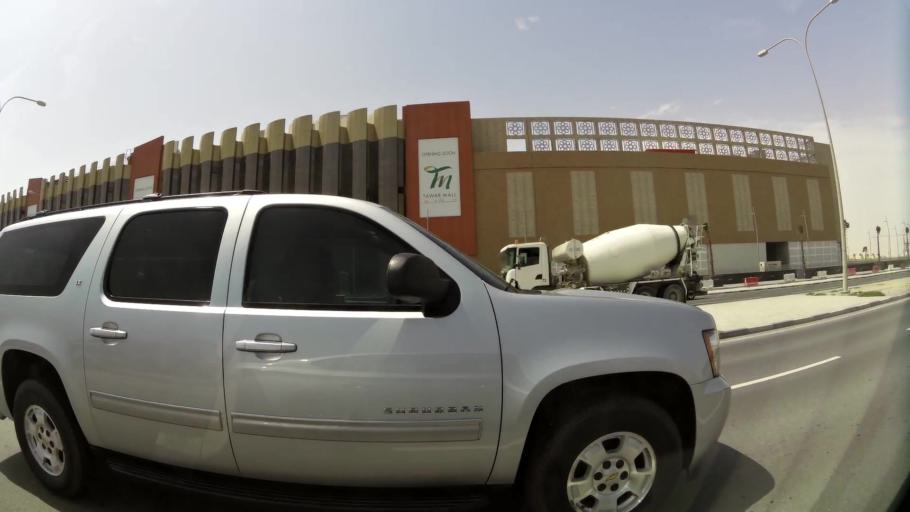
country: QA
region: Baladiyat ad Dawhah
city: Doha
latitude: 25.3369
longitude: 51.4814
